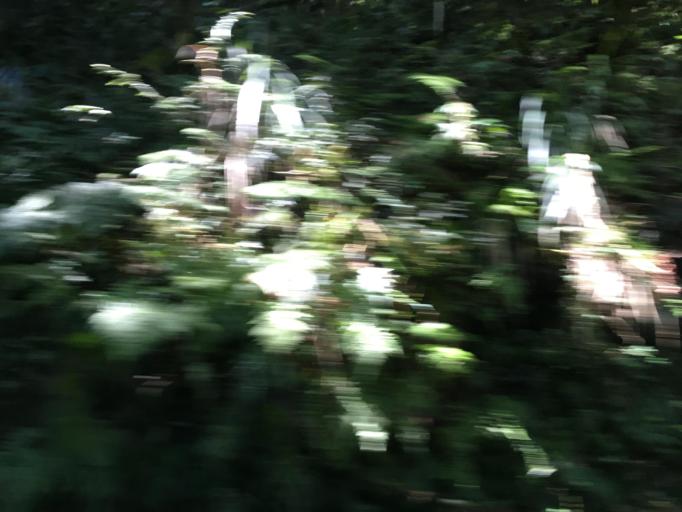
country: TW
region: Taiwan
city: Daxi
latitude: 24.5859
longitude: 121.4116
